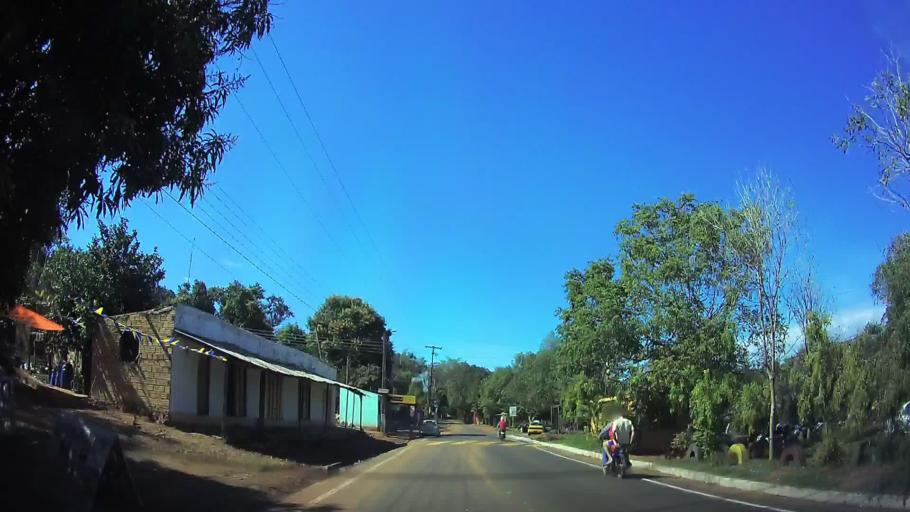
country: PY
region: Central
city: Aregua
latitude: -25.2576
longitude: -57.4528
